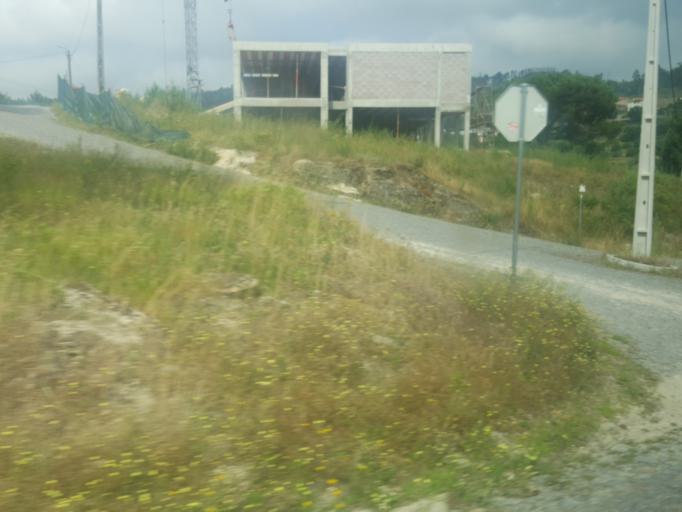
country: PT
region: Porto
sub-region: Marco de Canaveses
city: Marco de Canavezes
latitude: 41.1776
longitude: -8.1918
